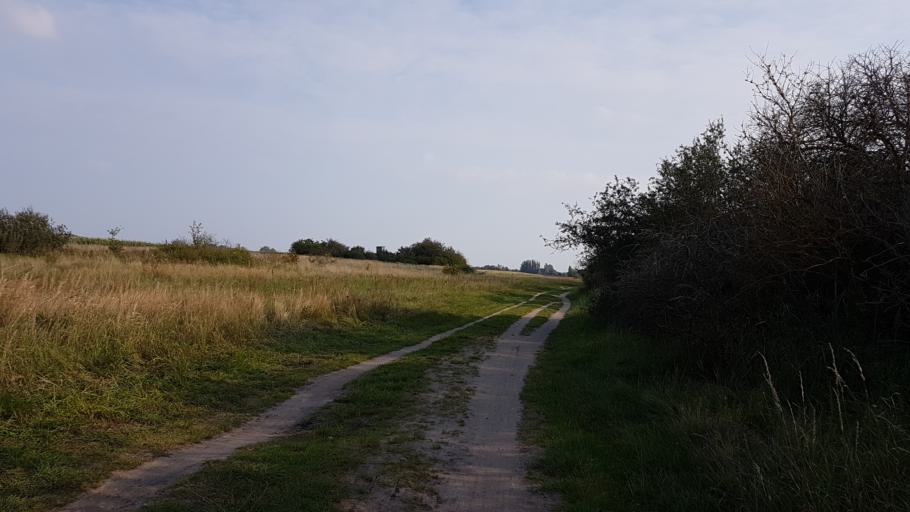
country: DE
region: Mecklenburg-Vorpommern
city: Glowe
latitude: 54.5559
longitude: 13.4980
